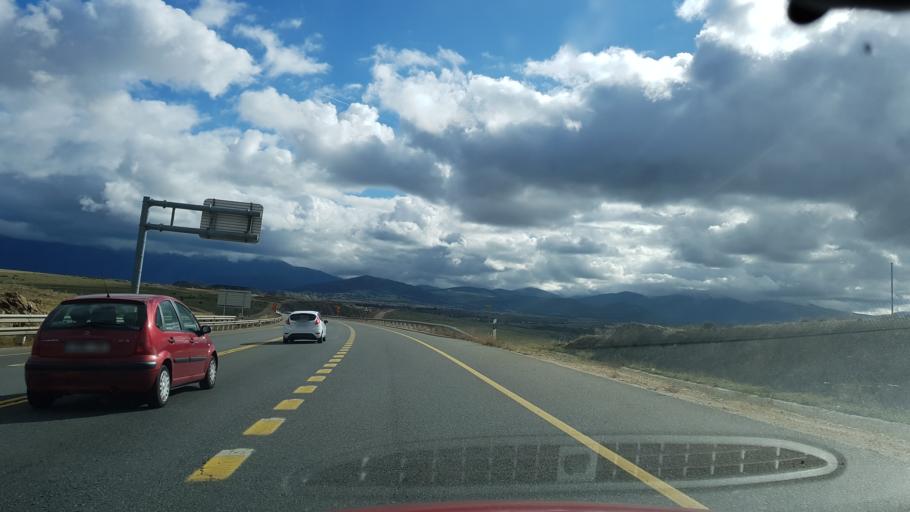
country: ES
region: Castille and Leon
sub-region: Provincia de Segovia
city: San Cristobal de Segovia
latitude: 40.9498
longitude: -4.0896
